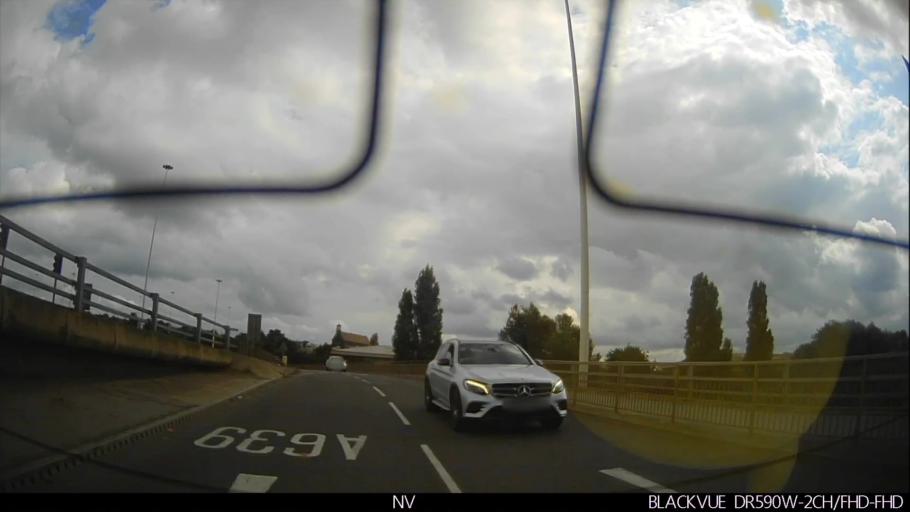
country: GB
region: England
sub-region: City and Borough of Leeds
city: Leeds
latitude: 53.7865
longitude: -1.5255
